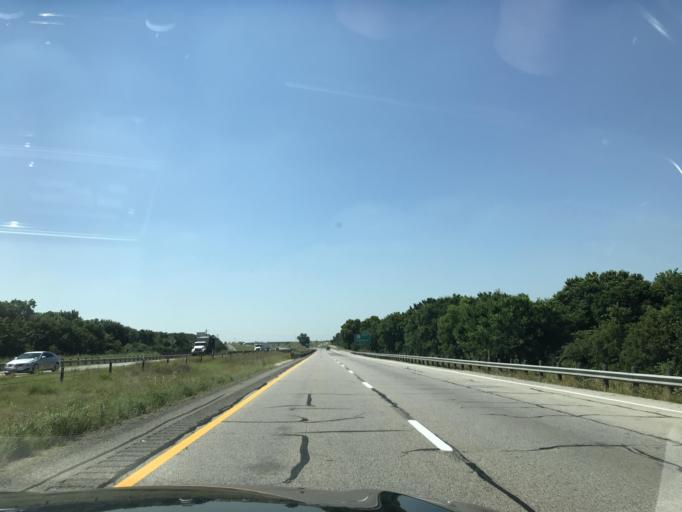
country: US
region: Texas
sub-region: Johnson County
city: Grandview
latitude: 32.2940
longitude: -97.1798
